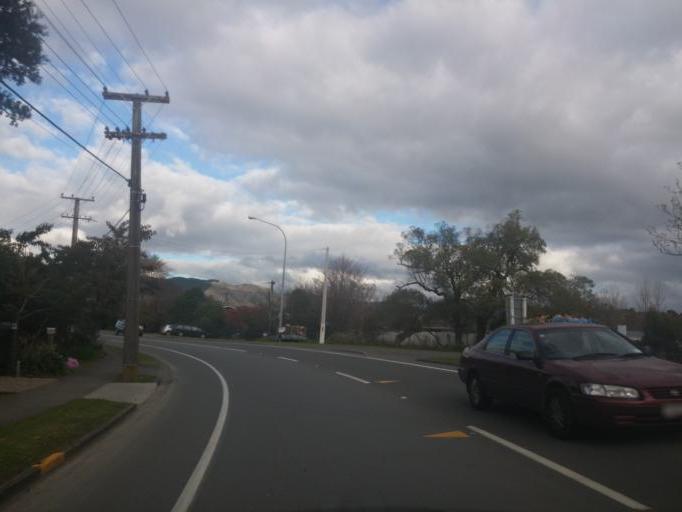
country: NZ
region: Wellington
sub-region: Kapiti Coast District
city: Paraparaumu
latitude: -40.8716
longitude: 175.0357
